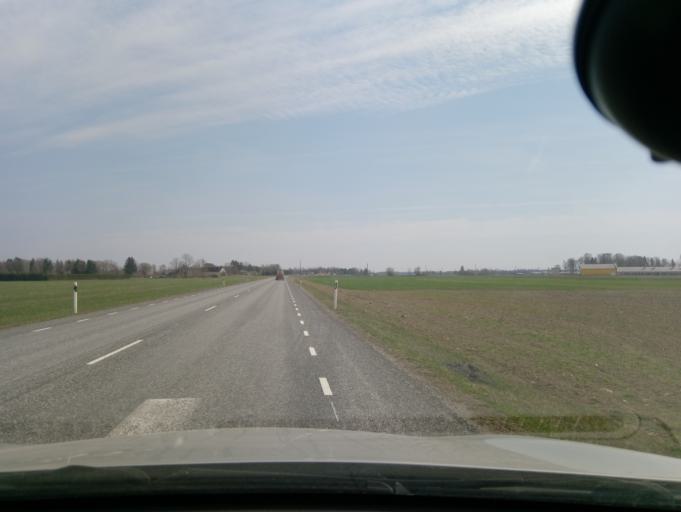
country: EE
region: Jaervamaa
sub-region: Tueri vald
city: Sarevere
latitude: 58.7646
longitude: 25.5395
